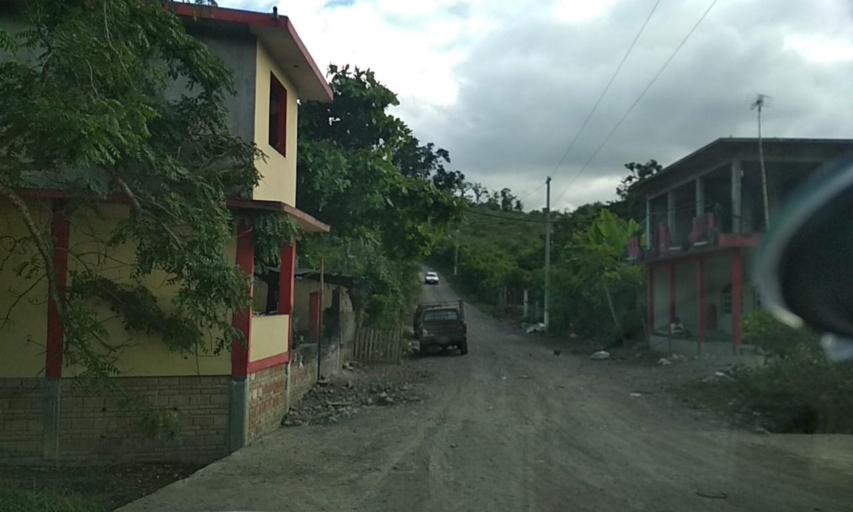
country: MX
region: Veracruz
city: Cazones de Herrera
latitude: 20.6478
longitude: -97.3383
